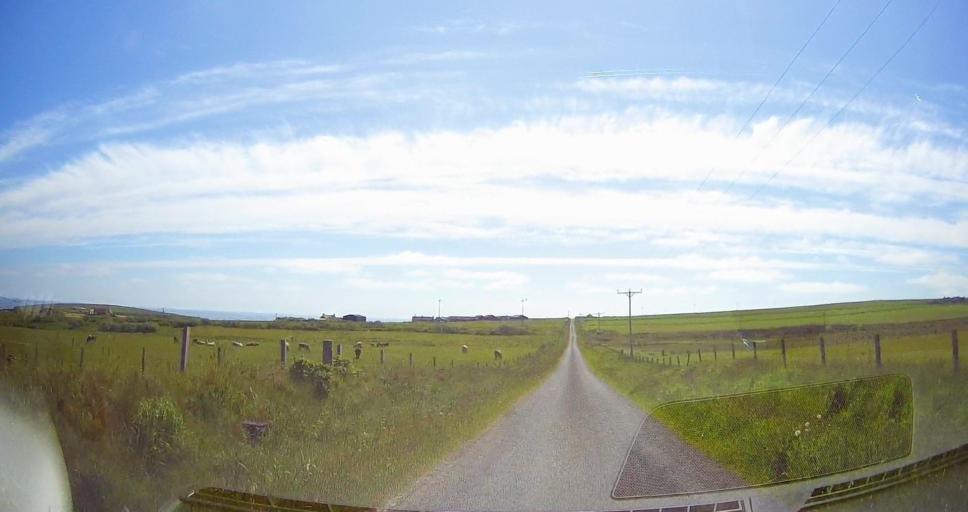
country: GB
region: Scotland
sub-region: Orkney Islands
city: Kirkwall
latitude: 58.8253
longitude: -2.9100
